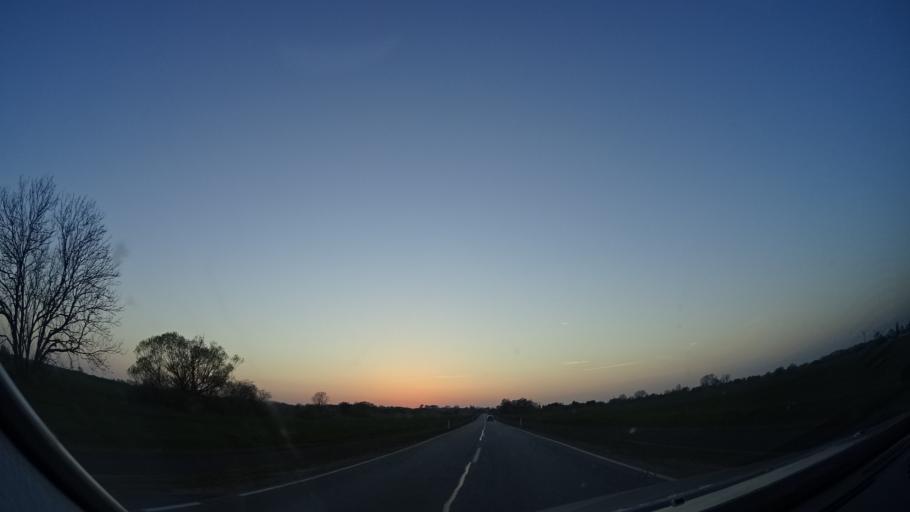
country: DK
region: Zealand
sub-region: Lejre Kommune
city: Ejby
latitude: 55.6639
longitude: 11.9004
